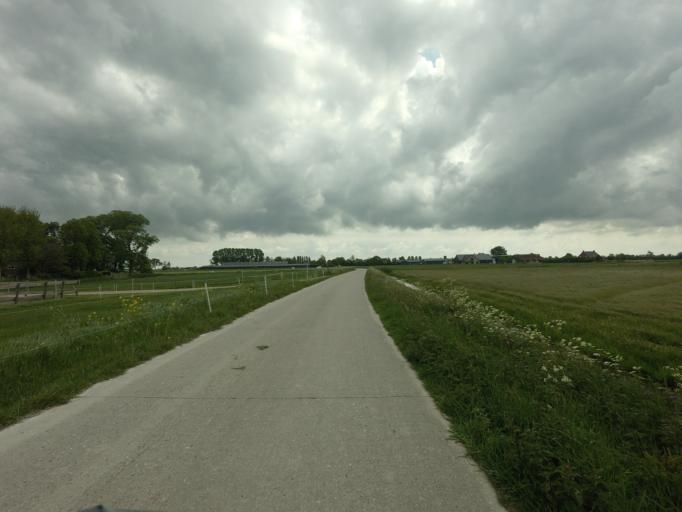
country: NL
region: Friesland
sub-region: Gemeente Littenseradiel
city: Wommels
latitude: 53.1063
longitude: 5.6220
